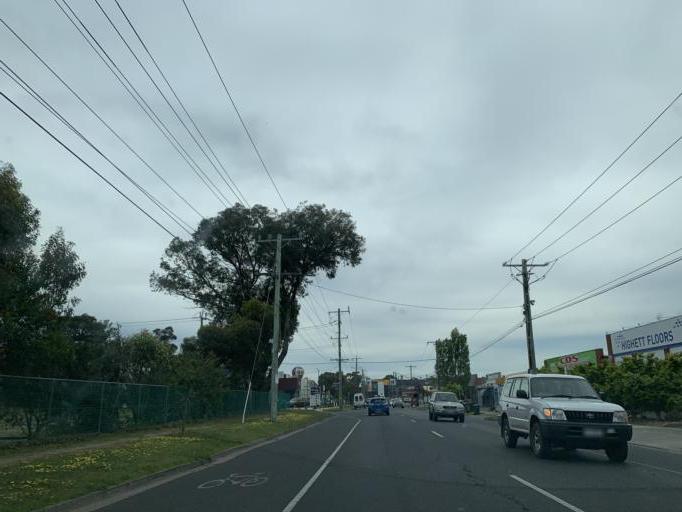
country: AU
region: Victoria
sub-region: Bayside
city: Highett
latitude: -37.9594
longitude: 145.0382
